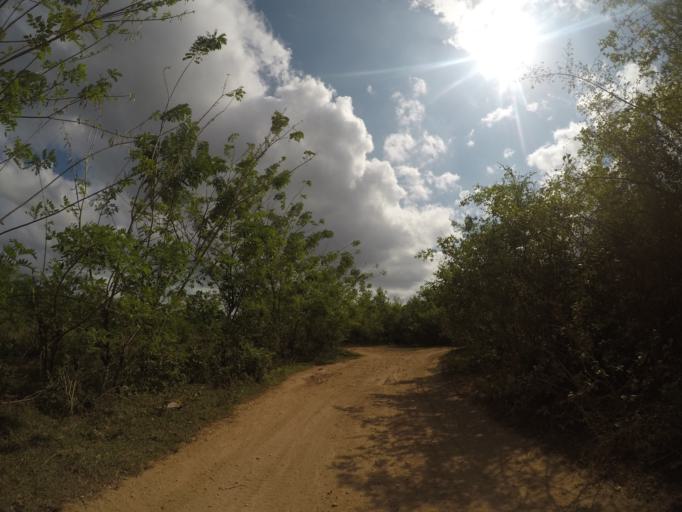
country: TZ
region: Zanzibar Central/South
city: Koani
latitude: -6.1911
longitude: 39.3148
